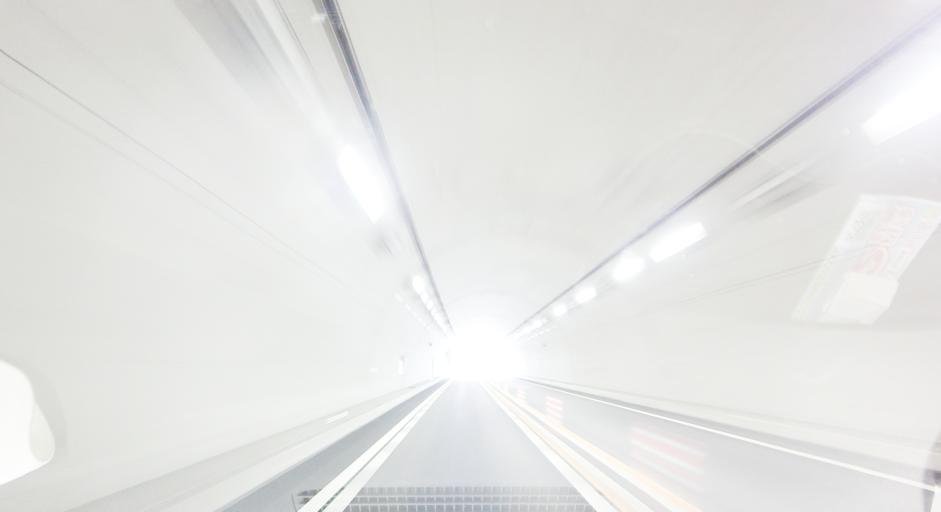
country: JP
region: Fukushima
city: Namie
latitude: 37.5933
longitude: 140.9273
